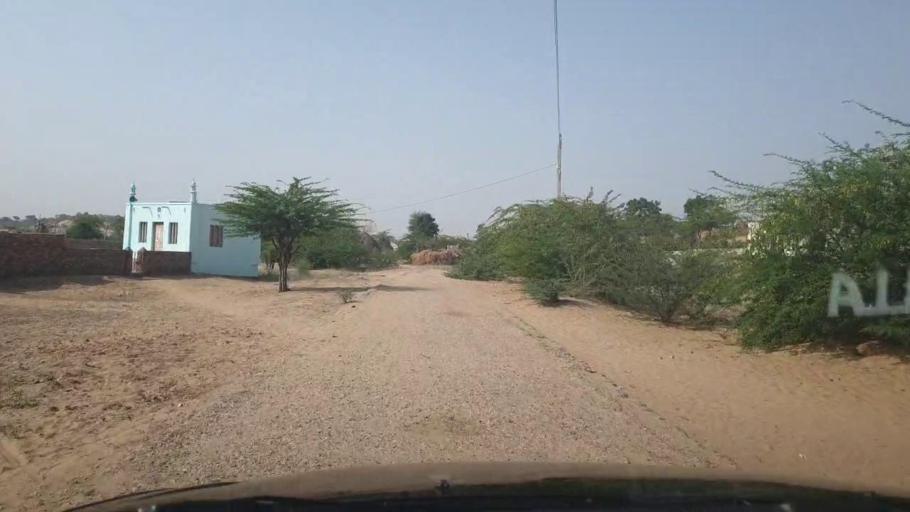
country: PK
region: Sindh
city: Islamkot
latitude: 25.0069
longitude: 70.2096
